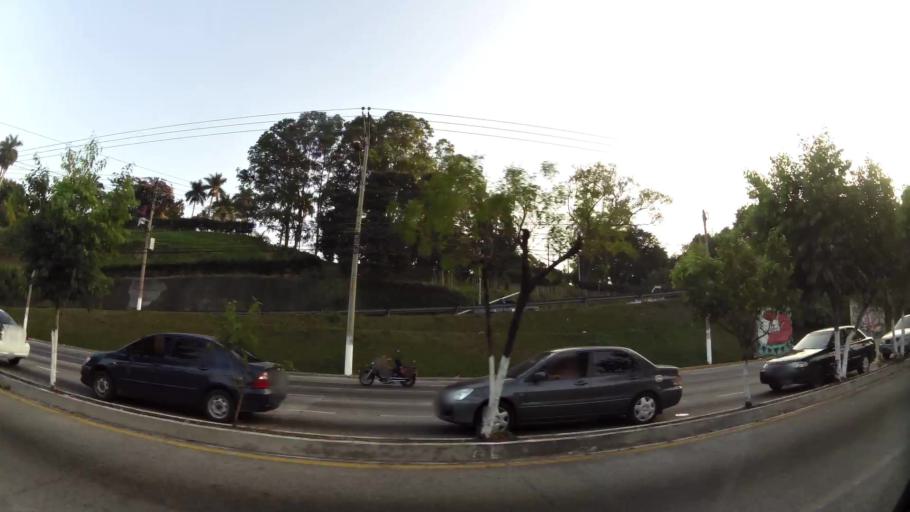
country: SV
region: San Salvador
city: San Salvador
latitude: 13.6791
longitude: -89.2114
